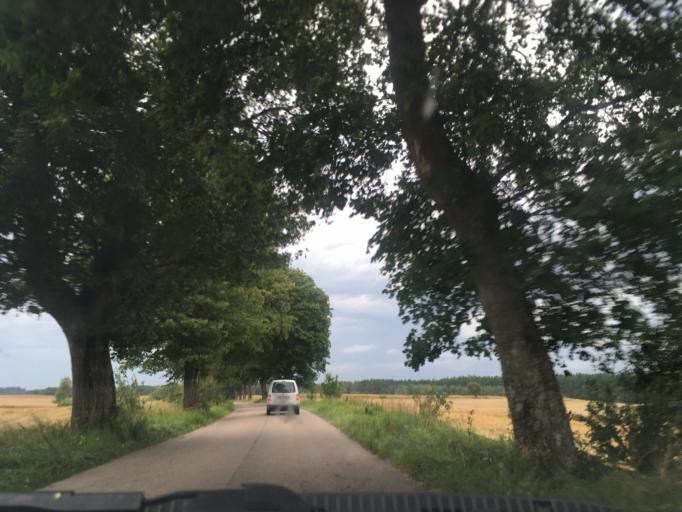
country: PL
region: Warmian-Masurian Voivodeship
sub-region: Powiat wegorzewski
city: Pozezdrze
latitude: 54.1368
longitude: 21.8451
